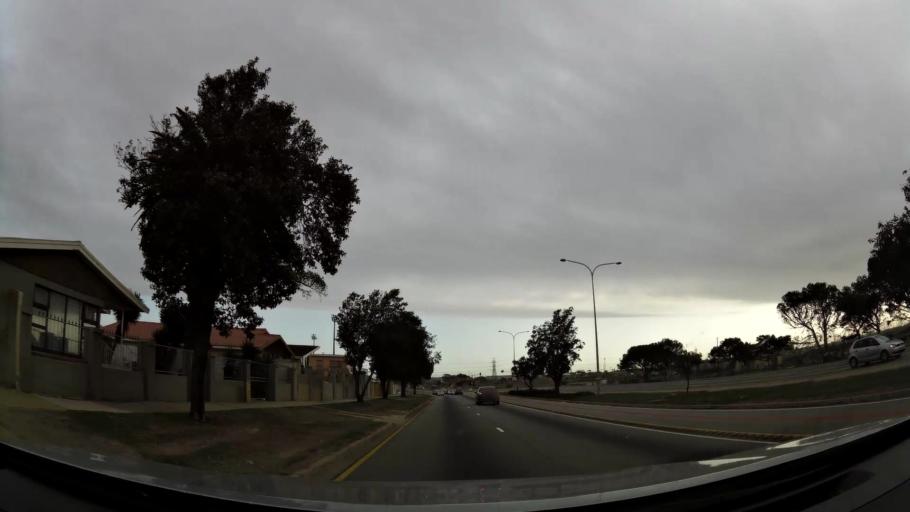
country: ZA
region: Eastern Cape
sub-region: Nelson Mandela Bay Metropolitan Municipality
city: Port Elizabeth
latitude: -33.9163
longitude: 25.5632
